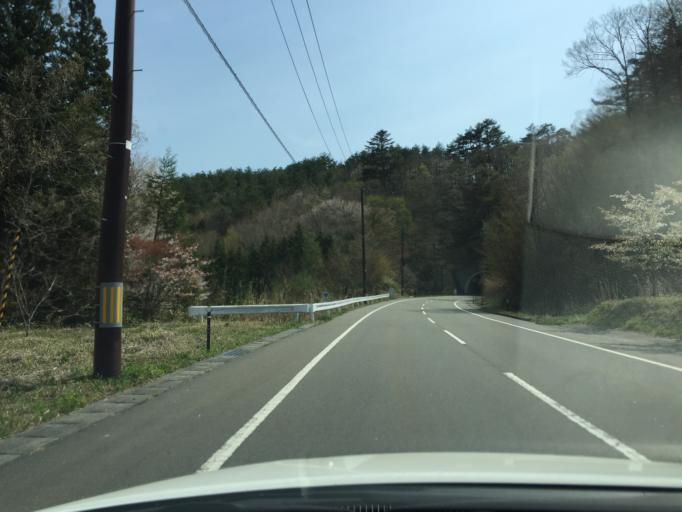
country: JP
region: Fukushima
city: Iwaki
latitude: 37.2841
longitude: 140.8425
